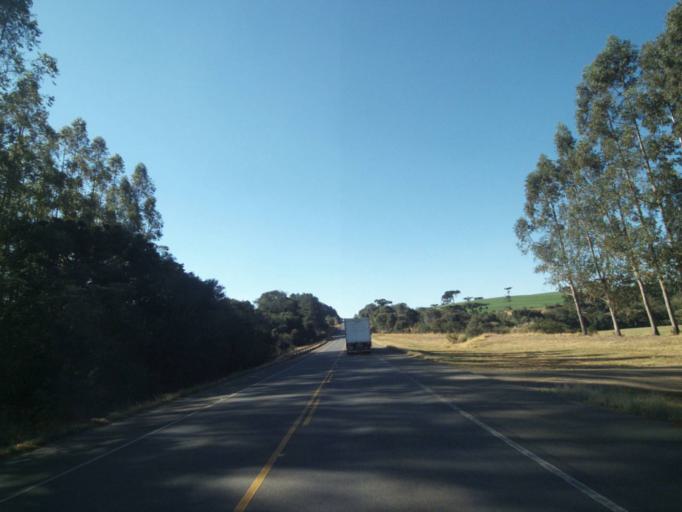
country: BR
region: Parana
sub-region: Tibagi
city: Tibagi
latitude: -24.5483
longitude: -50.4523
